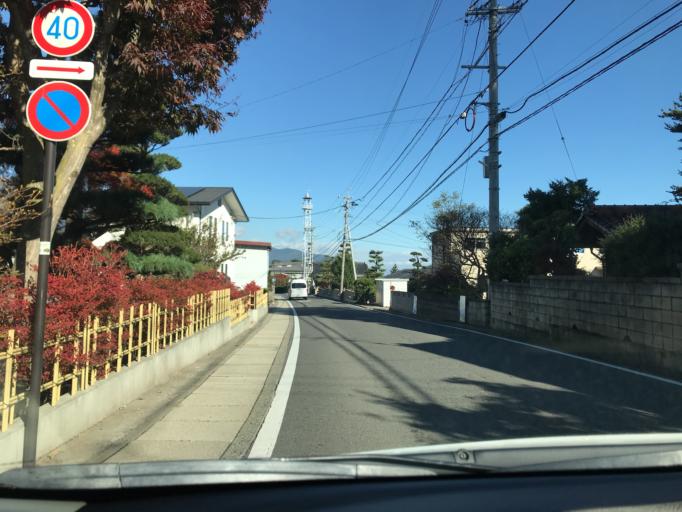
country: JP
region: Nagano
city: Toyoshina
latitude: 36.1897
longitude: 137.8552
